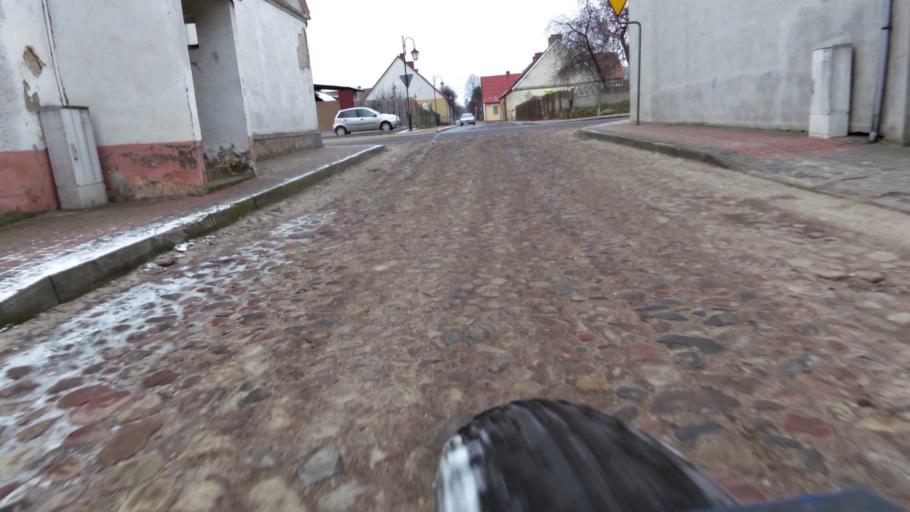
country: PL
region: West Pomeranian Voivodeship
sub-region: Powiat walecki
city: Miroslawiec
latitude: 53.3403
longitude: 16.0938
